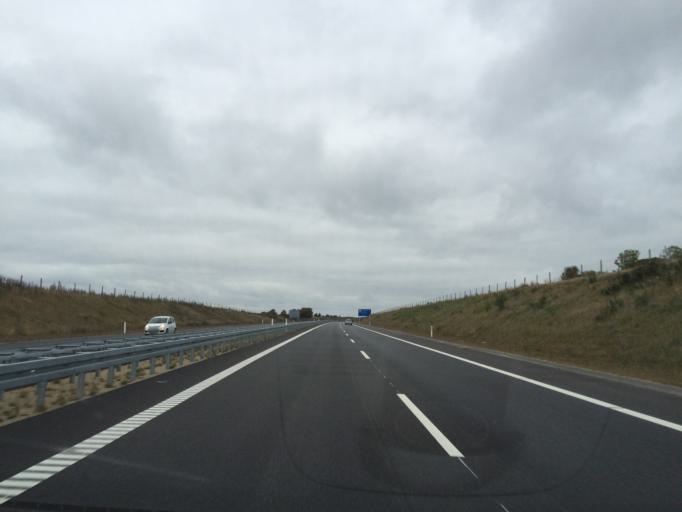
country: DK
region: Central Jutland
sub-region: Silkeborg Kommune
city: Silkeborg
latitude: 56.1921
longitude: 9.4980
